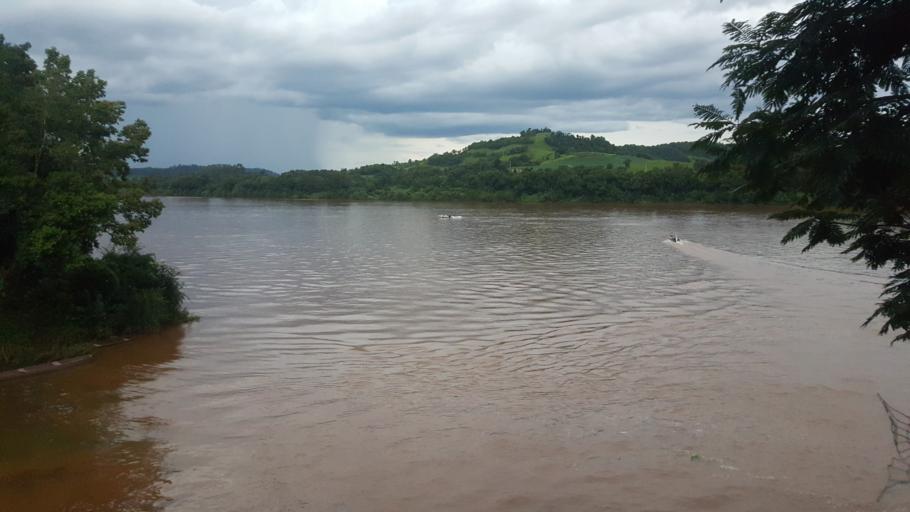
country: BR
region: Rio Grande do Sul
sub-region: Frederico Westphalen
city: Frederico Westphalen
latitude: -27.1066
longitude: -53.3949
